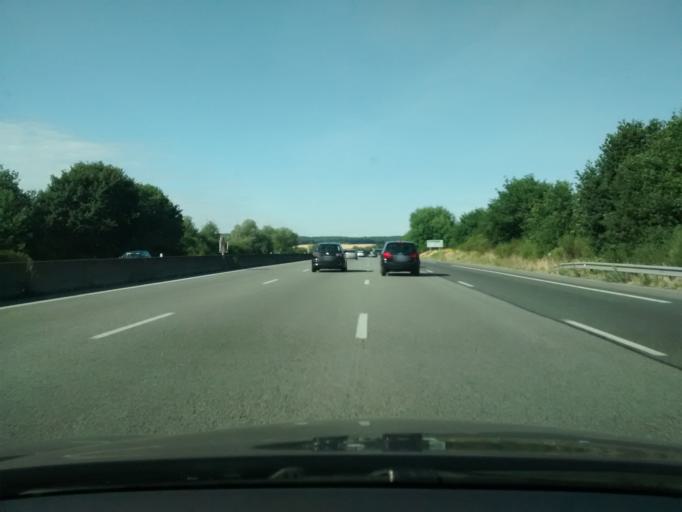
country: FR
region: Ile-de-France
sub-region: Departement de l'Essonne
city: Saint-Cyr-sous-Dourdan
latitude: 48.5811
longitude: 2.0143
